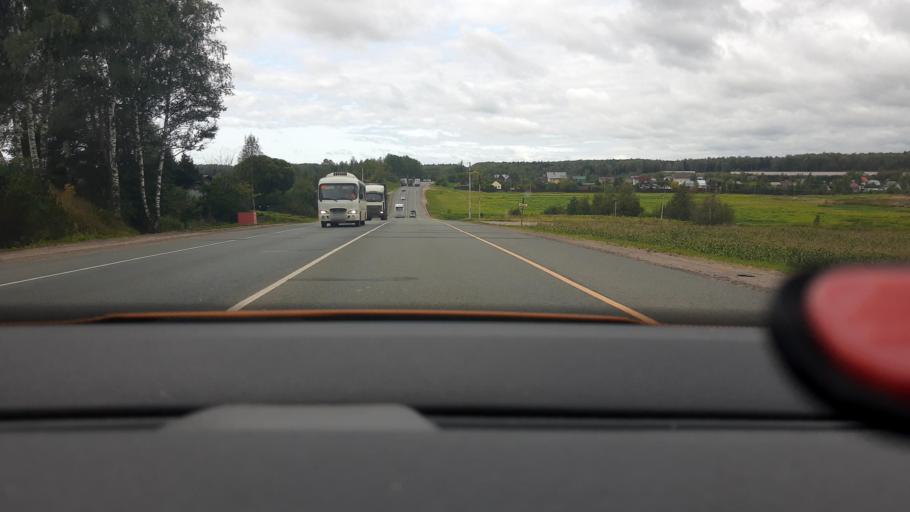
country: RU
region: Moskovskaya
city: Krasnoarmeysk
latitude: 56.0775
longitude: 38.0341
